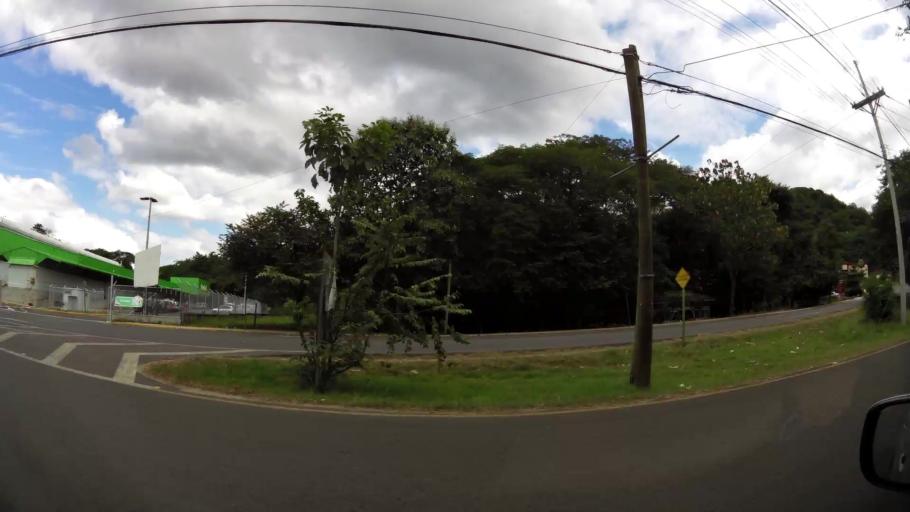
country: CR
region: Guanacaste
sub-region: Canton de Nicoya
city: Nicoya
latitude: 10.1603
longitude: -85.4488
